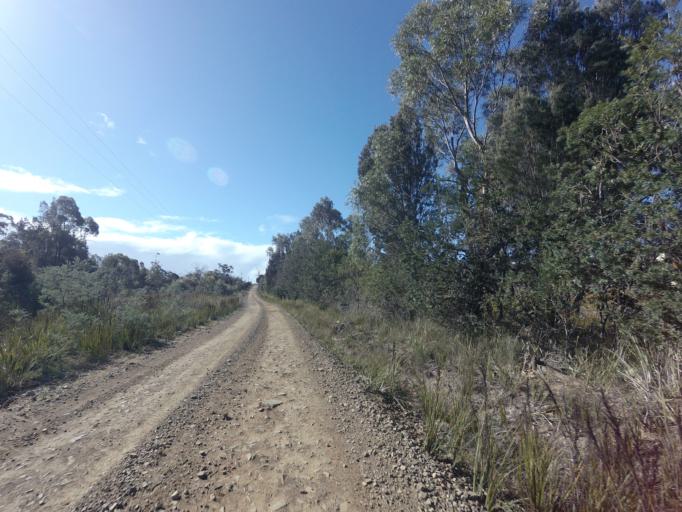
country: AU
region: Tasmania
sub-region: Sorell
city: Sorell
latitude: -42.3505
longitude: 147.9717
